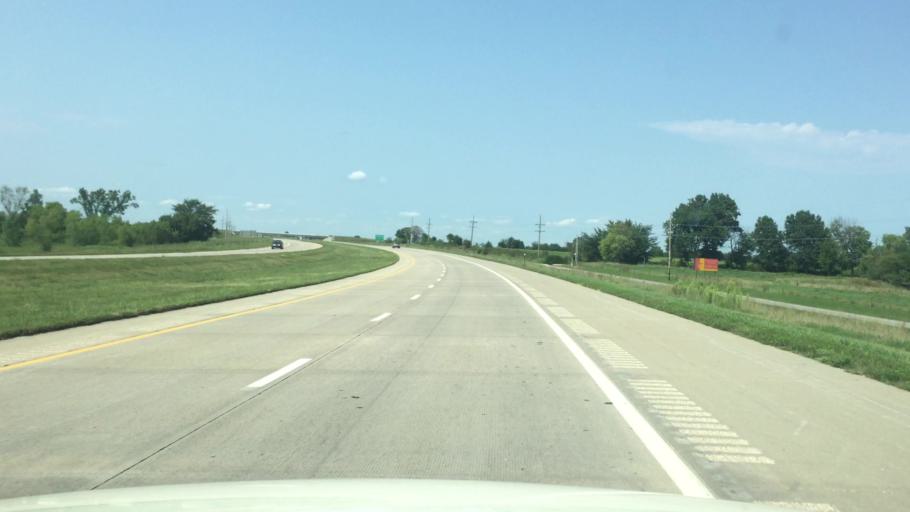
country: US
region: Kansas
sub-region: Linn County
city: Pleasanton
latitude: 38.1585
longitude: -94.6962
